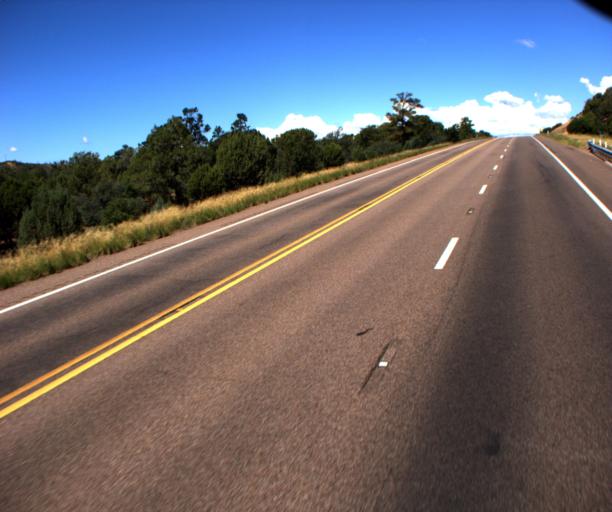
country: US
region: Arizona
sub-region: Navajo County
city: Linden
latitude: 34.2937
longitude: -110.1840
